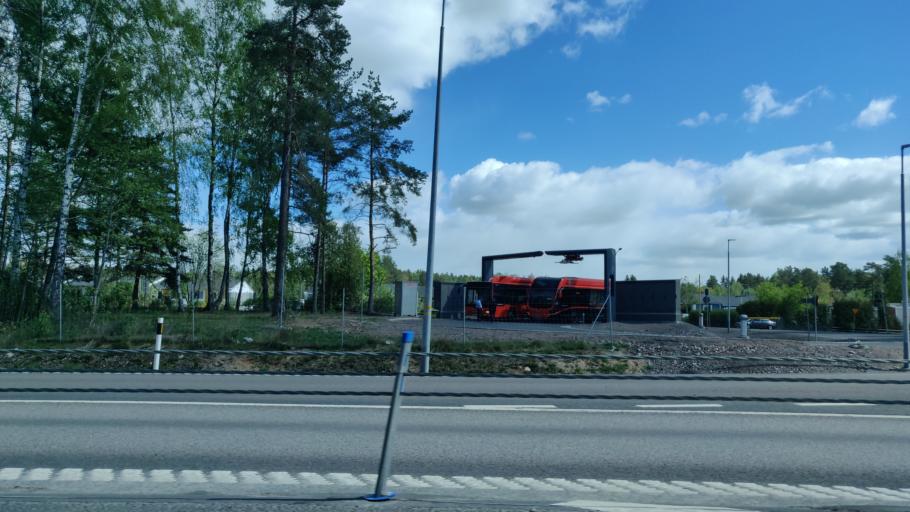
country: SE
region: Vaermland
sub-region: Karlstads Kommun
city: Karlstad
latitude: 59.4089
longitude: 13.5318
